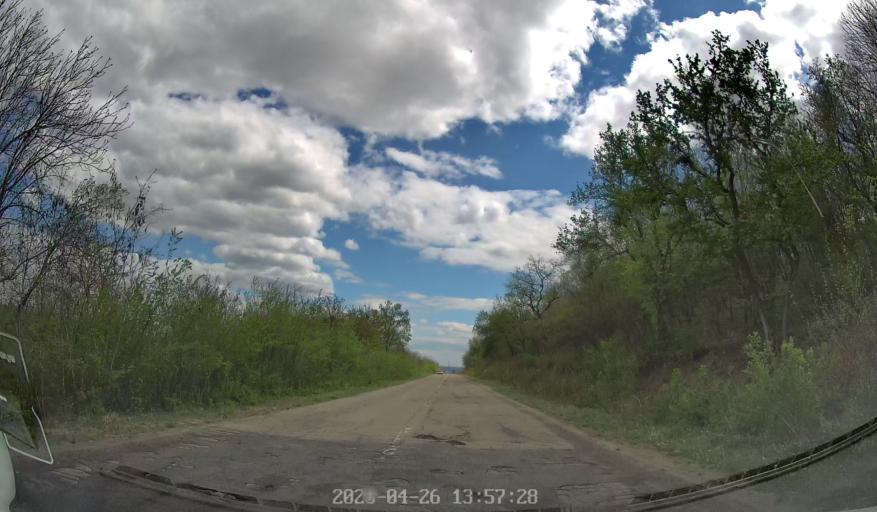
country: MD
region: Telenesti
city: Cocieri
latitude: 47.2741
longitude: 29.1161
